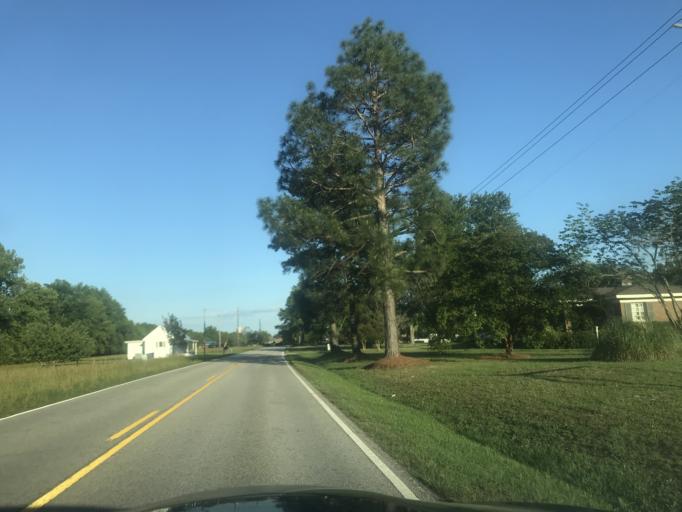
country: US
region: North Carolina
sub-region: Johnston County
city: Archer Lodge
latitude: 35.7004
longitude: -78.3812
